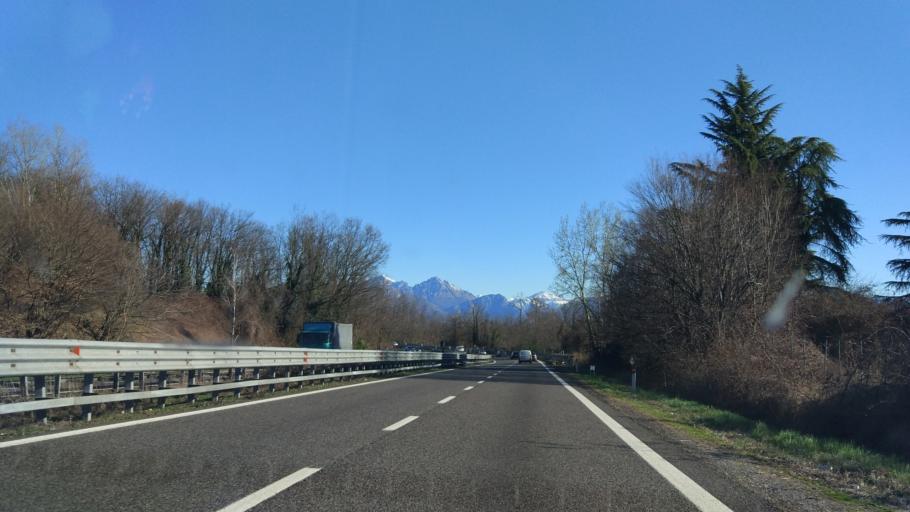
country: IT
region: Lombardy
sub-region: Provincia di Monza e Brianza
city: Verano Brianza
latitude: 45.6999
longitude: 9.2300
